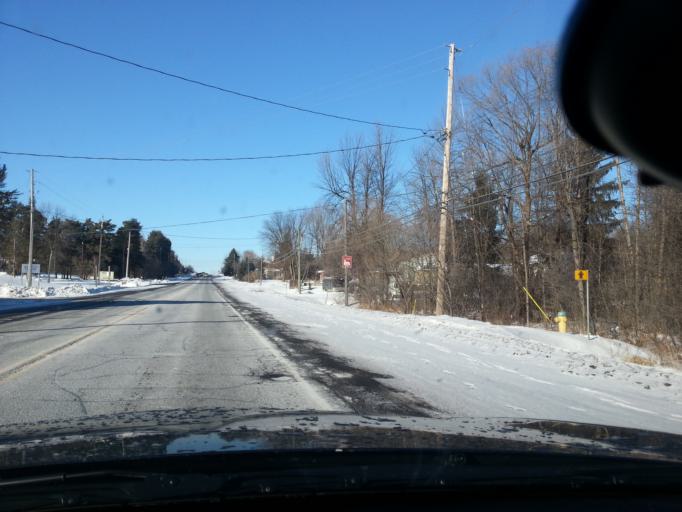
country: CA
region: Ontario
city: Ottawa
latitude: 45.2858
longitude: -75.5737
